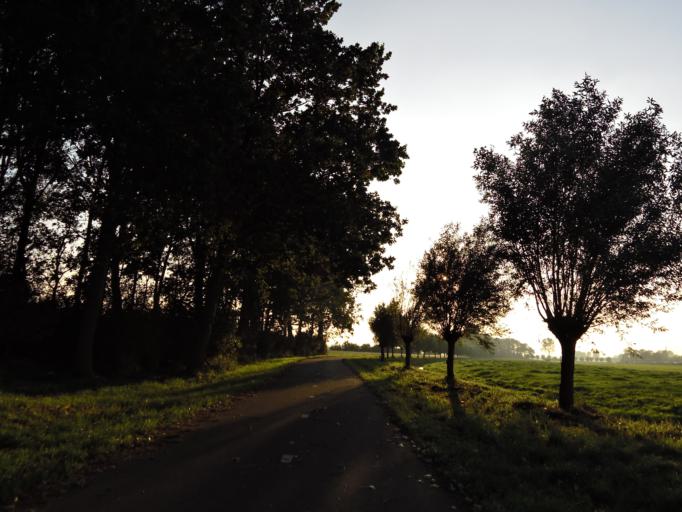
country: NL
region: South Holland
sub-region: Gemeente Kaag en Braassem
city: Oude Wetering
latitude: 52.1680
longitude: 4.6003
